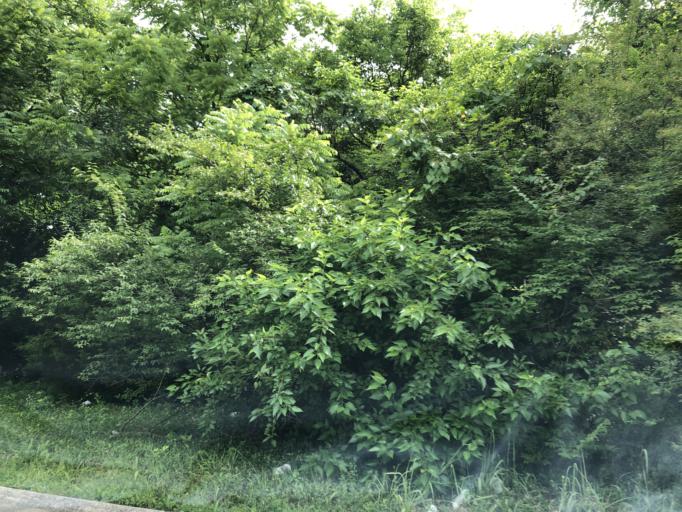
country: US
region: Tennessee
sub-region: Davidson County
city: Goodlettsville
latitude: 36.2860
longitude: -86.7158
